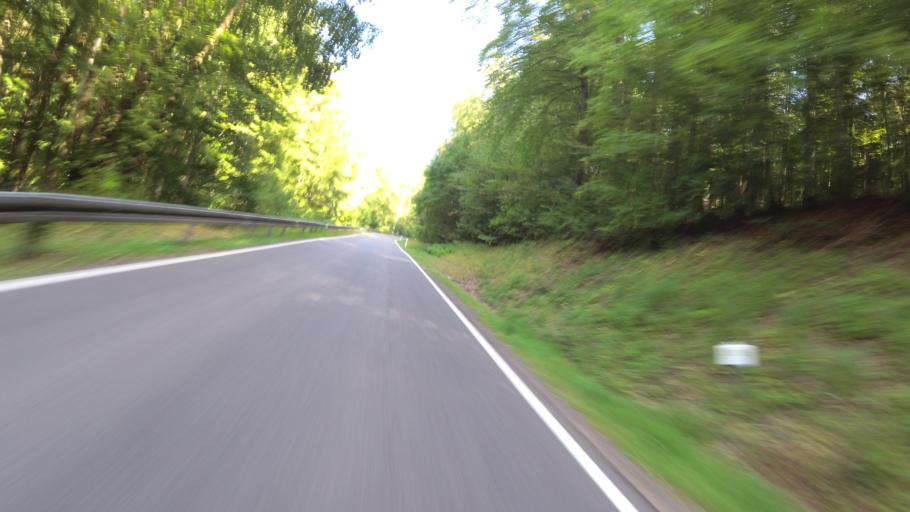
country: DE
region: Saarland
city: Gersheim
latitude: 49.1350
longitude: 7.2408
